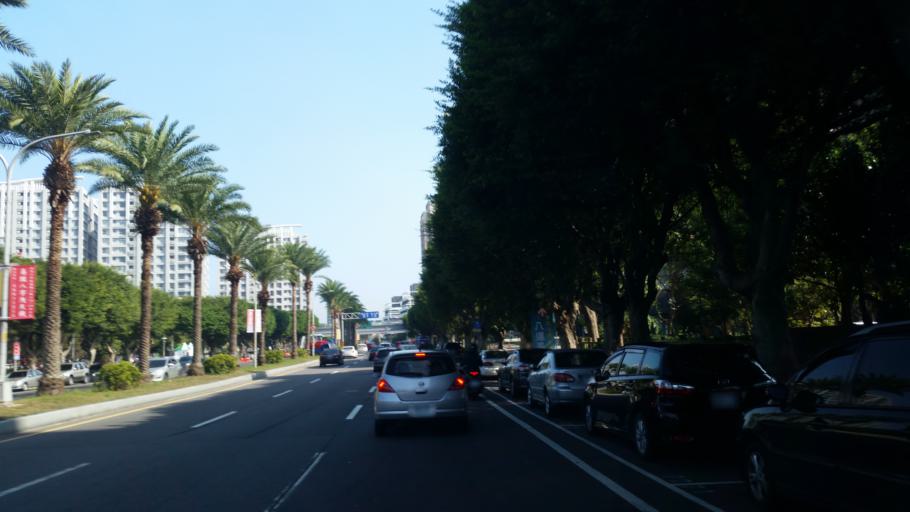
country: TW
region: Taiwan
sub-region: Taoyuan
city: Taoyuan
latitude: 25.0730
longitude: 121.3759
